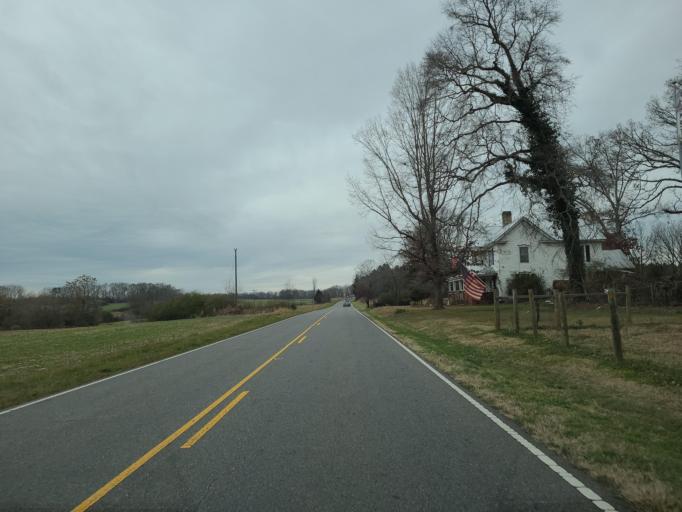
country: US
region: North Carolina
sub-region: Cleveland County
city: Shelby
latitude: 35.3651
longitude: -81.5787
